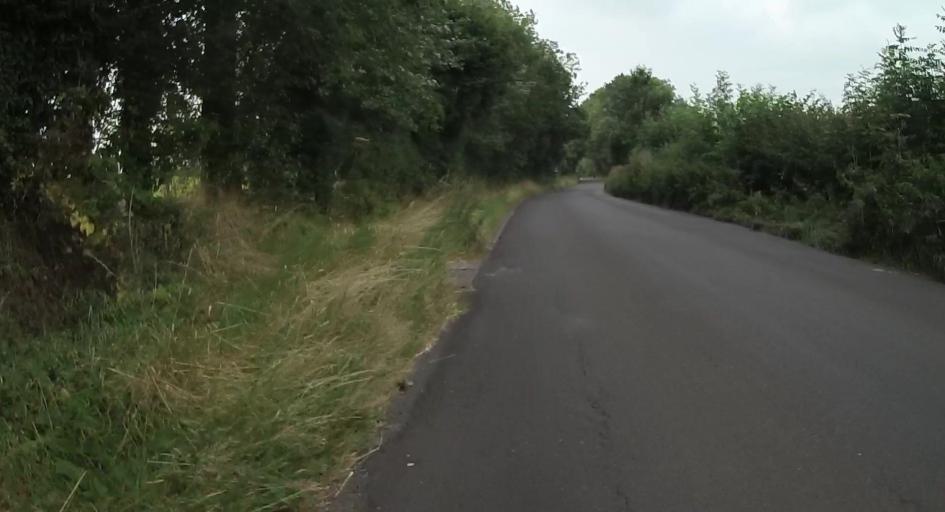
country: GB
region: England
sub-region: Hampshire
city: Old Basing
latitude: 51.2540
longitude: -1.0430
